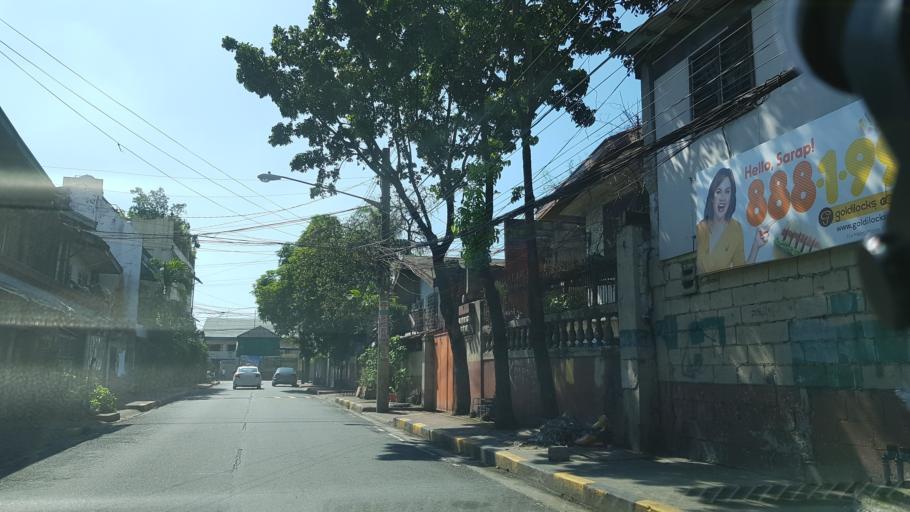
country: PH
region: Calabarzon
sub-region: Province of Rizal
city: Pateros
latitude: 14.5620
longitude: 121.0699
